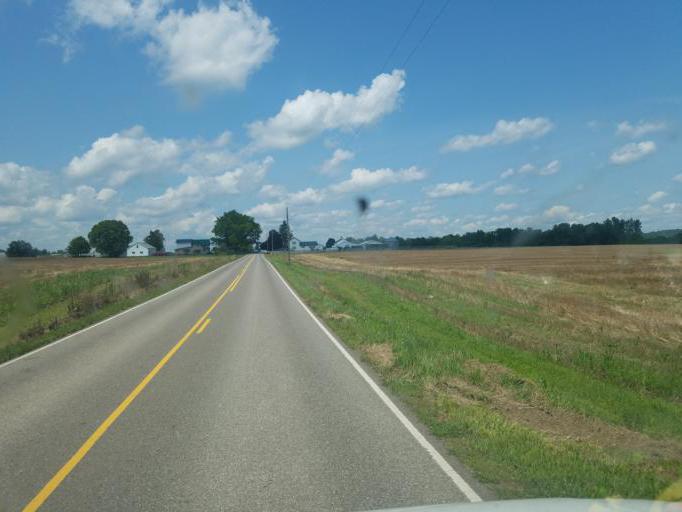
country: US
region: Ohio
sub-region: Knox County
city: Fredericktown
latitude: 40.5276
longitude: -82.5984
